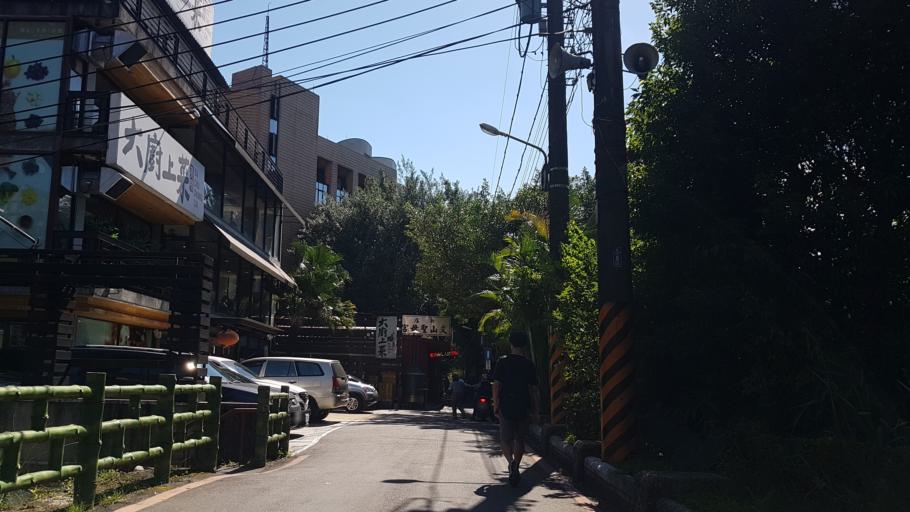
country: TW
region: Taipei
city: Taipei
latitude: 24.9602
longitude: 121.5371
